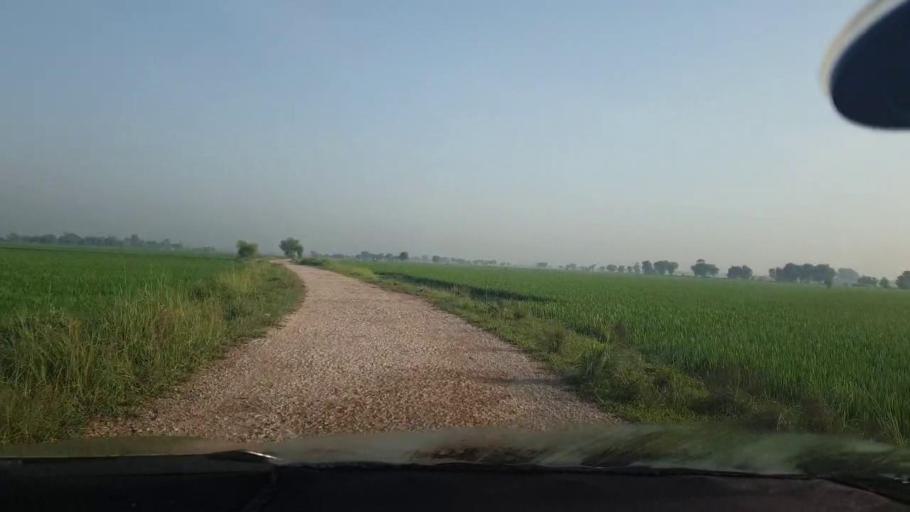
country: PK
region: Sindh
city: Kambar
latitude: 27.6223
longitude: 68.0179
